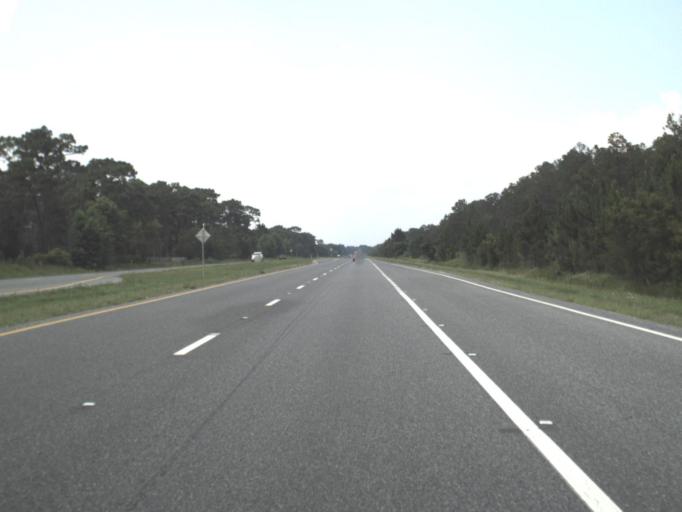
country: US
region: Florida
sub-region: Putnam County
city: Palatka
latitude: 29.7470
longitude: -81.6421
